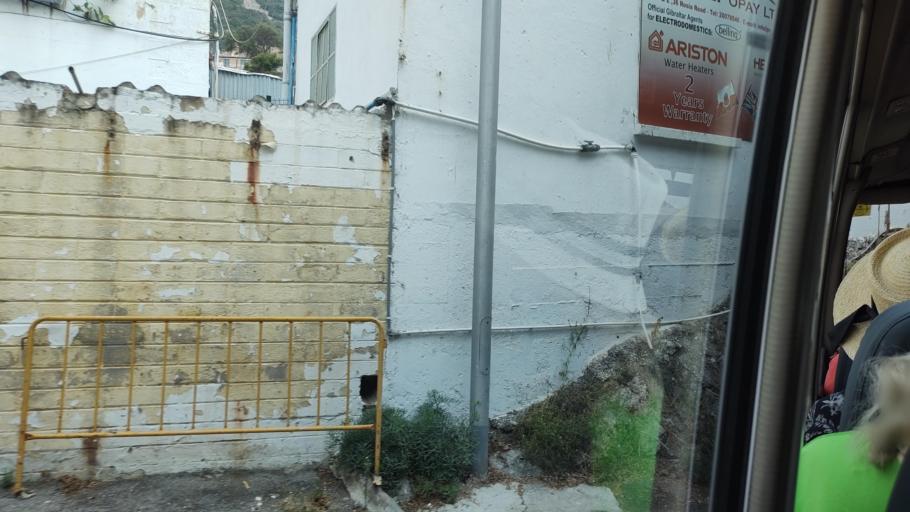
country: GI
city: Gibraltar
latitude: 36.1204
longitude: -5.3519
